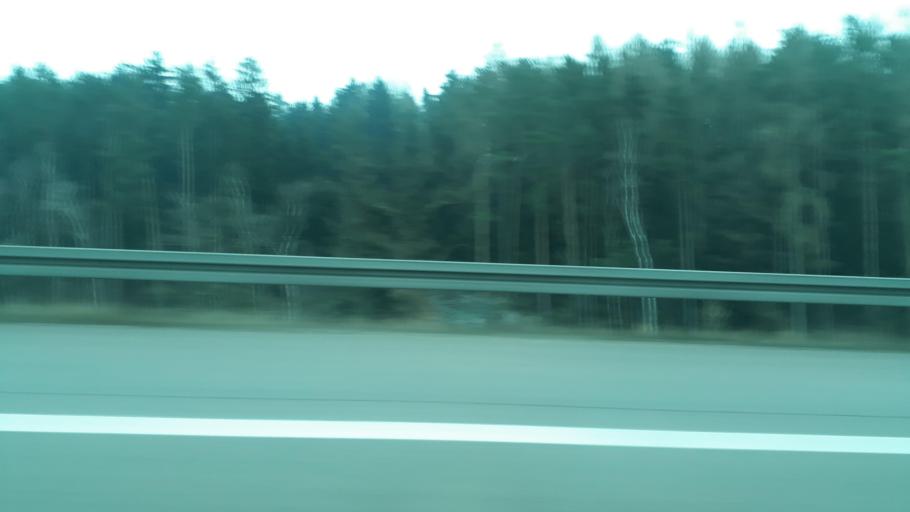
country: DE
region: Bavaria
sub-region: Upper Palatinate
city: Stulln
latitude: 49.4569
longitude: 12.1306
